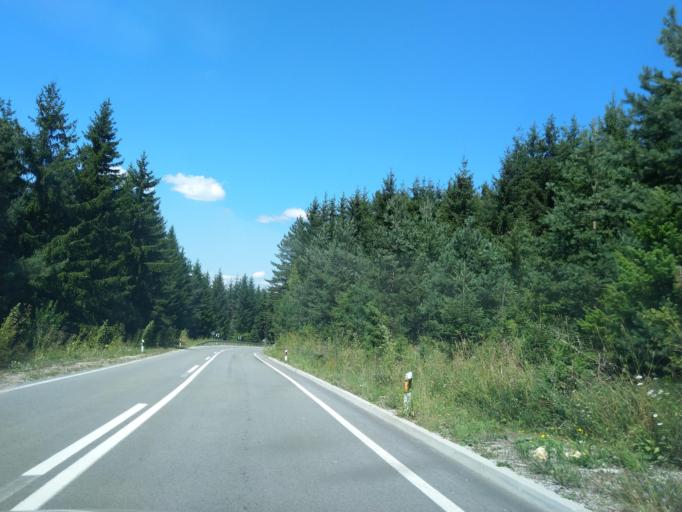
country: RS
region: Central Serbia
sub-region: Zlatiborski Okrug
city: Sjenica
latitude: 43.3159
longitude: 19.8926
